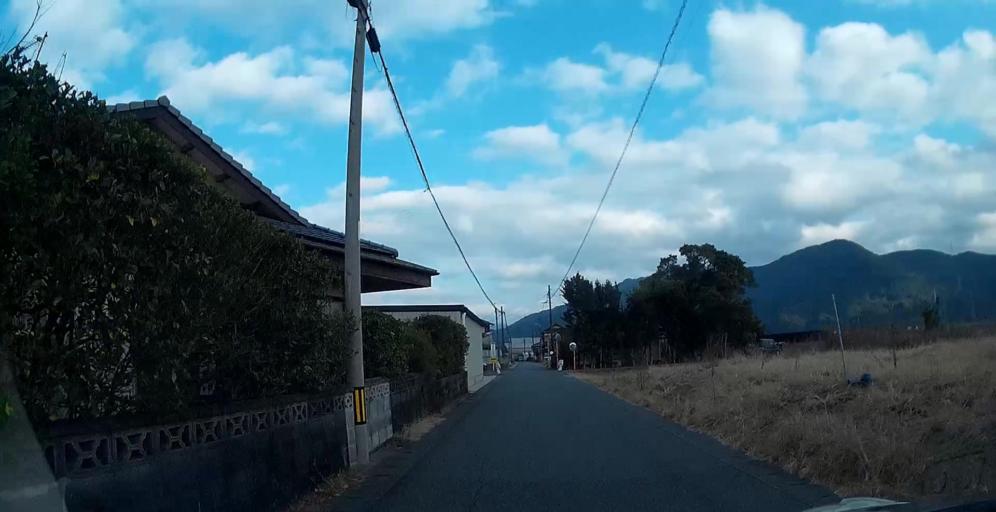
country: JP
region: Kumamoto
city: Yatsushiro
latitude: 32.5312
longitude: 130.6414
